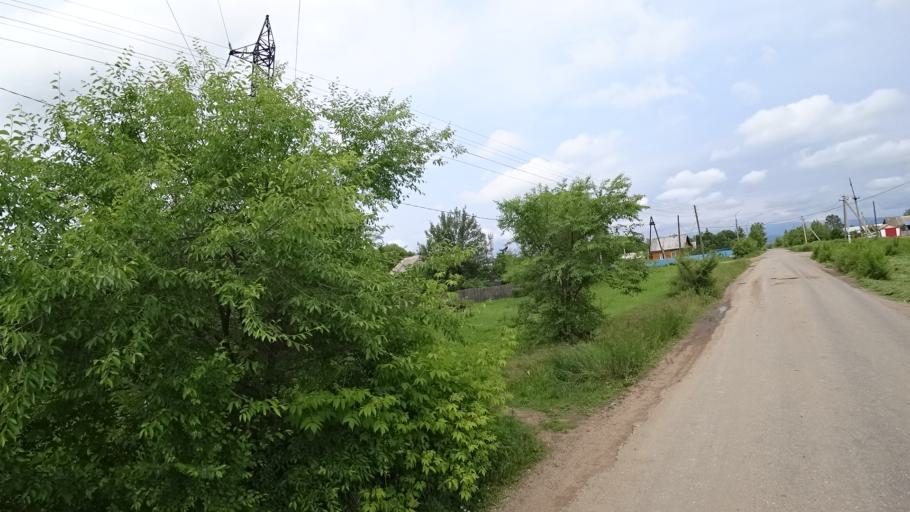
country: RU
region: Primorskiy
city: Novosysoyevka
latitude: 44.2318
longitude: 133.3603
